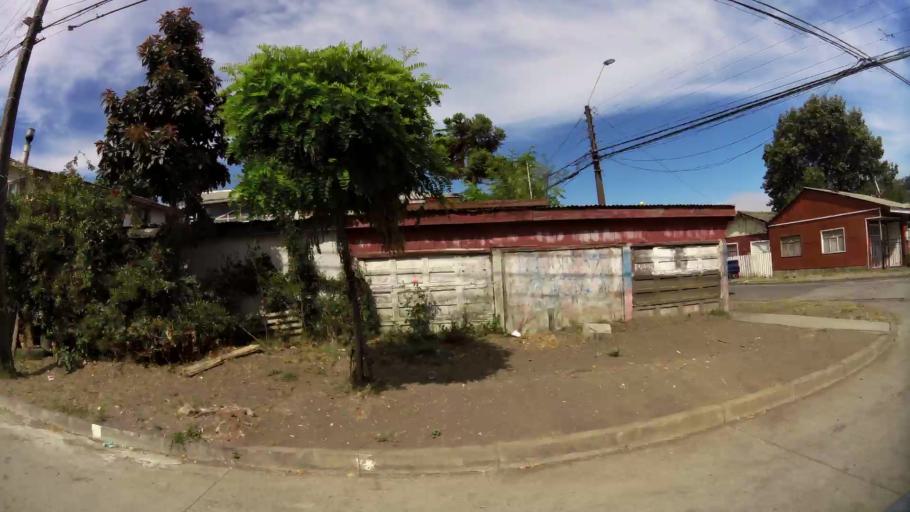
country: CL
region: Biobio
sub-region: Provincia de Concepcion
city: Talcahuano
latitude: -36.7240
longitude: -73.1240
